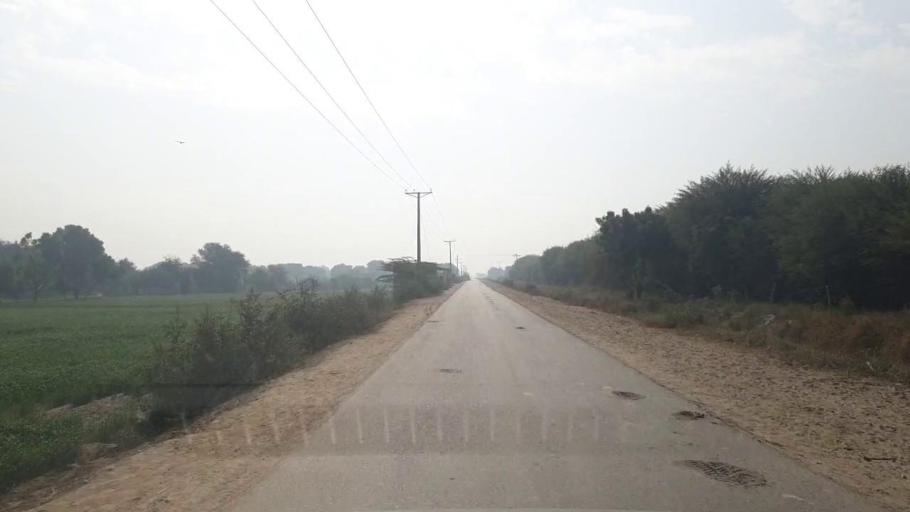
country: PK
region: Sindh
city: Hala
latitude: 25.7949
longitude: 68.4391
